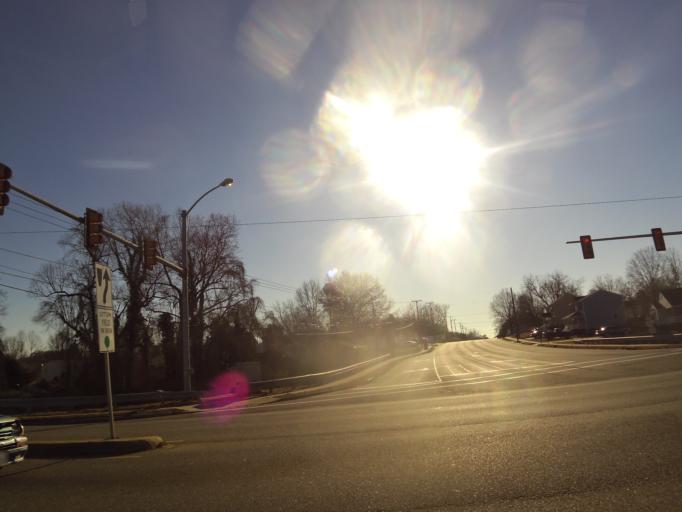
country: US
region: Virginia
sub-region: City of Hopewell
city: Hopewell
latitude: 37.2847
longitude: -77.2994
